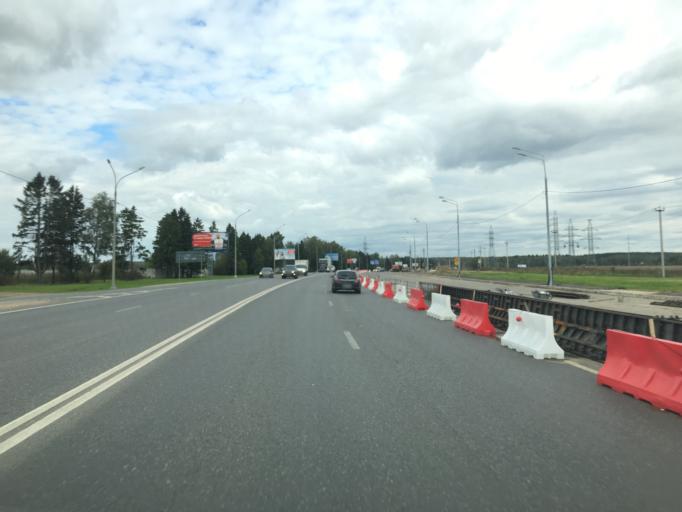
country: RU
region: Moskovskaya
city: Filimonki
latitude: 55.5309
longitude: 37.3896
